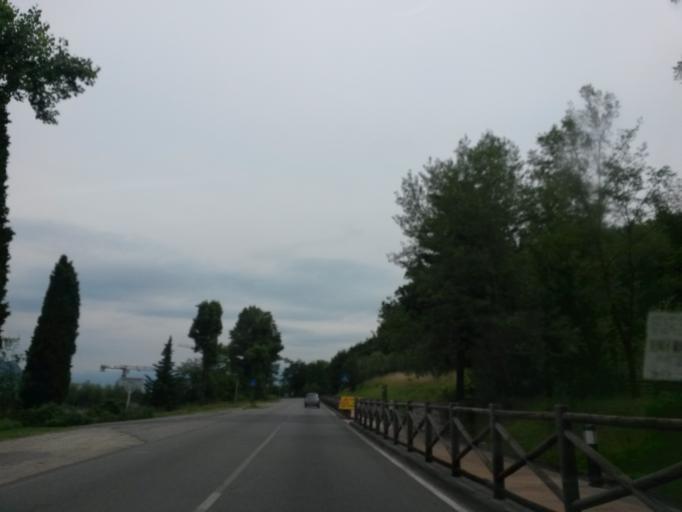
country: IT
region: Lombardy
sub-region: Provincia di Brescia
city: Cunettone-Villa
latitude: 45.5932
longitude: 10.5135
